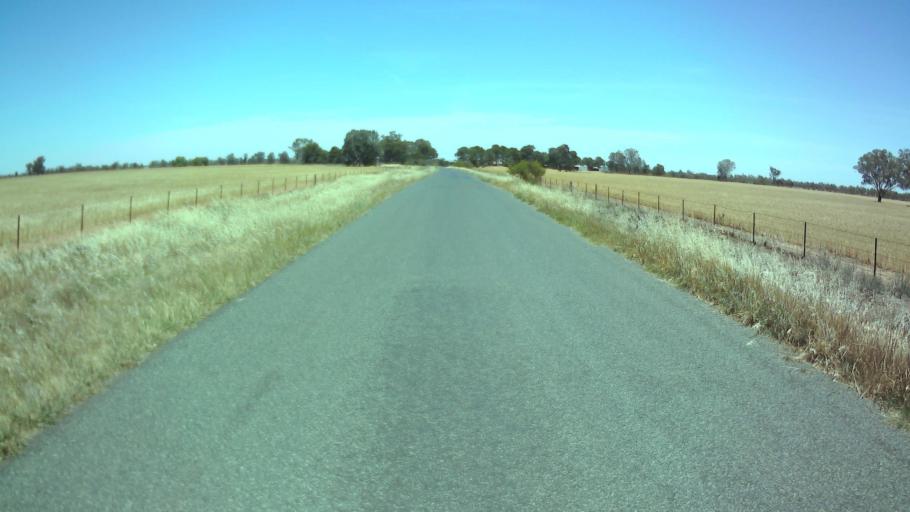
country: AU
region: New South Wales
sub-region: Weddin
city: Grenfell
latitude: -34.0435
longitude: 147.7859
